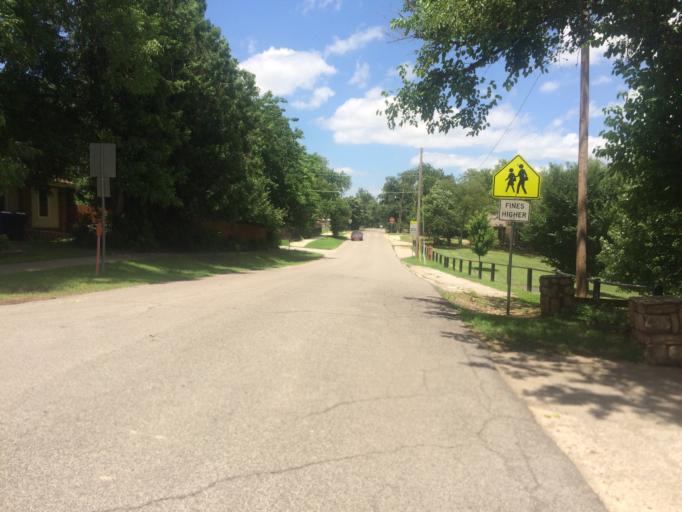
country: US
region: Oklahoma
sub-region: Cleveland County
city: Norman
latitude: 35.2133
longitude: -97.4346
